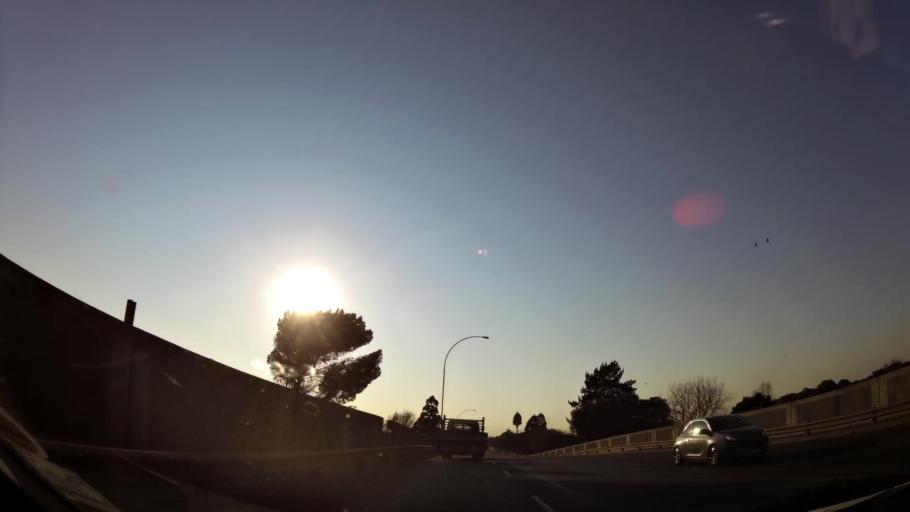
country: ZA
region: Gauteng
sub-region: Ekurhuleni Metropolitan Municipality
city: Germiston
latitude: -26.2233
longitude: 28.1631
